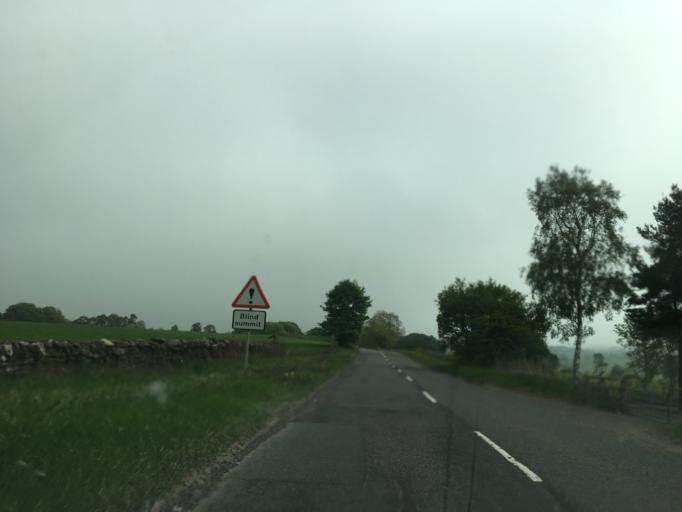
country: GB
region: Scotland
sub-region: The Scottish Borders
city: West Linton
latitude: 55.7124
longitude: -3.3485
